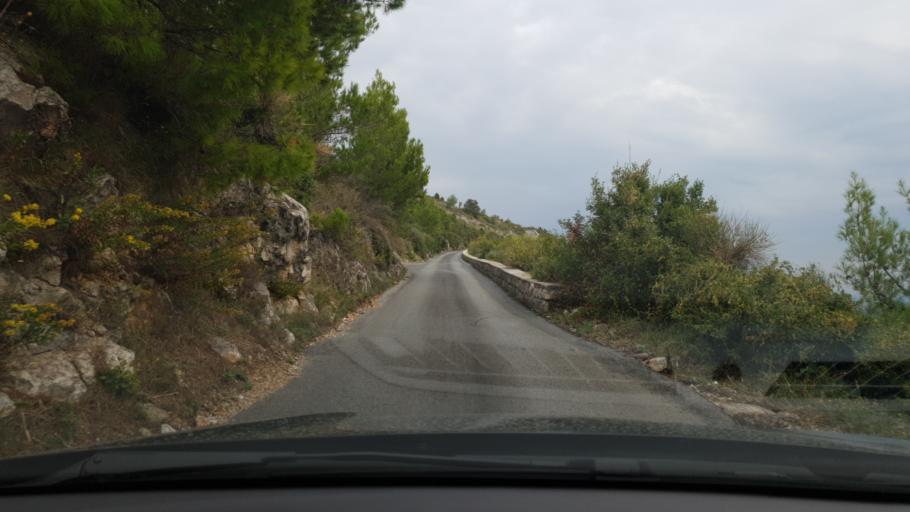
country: HR
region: Dubrovacko-Neretvanska
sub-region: Grad Dubrovnik
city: Dubrovnik
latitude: 42.6414
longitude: 18.1280
